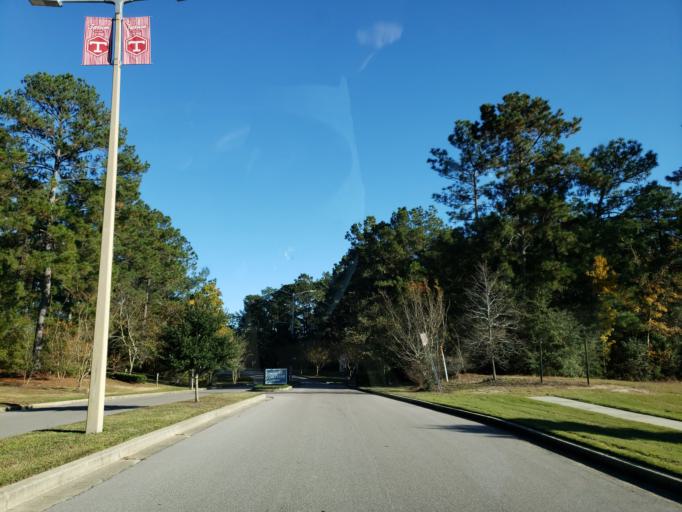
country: US
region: Mississippi
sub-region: Forrest County
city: Hattiesburg
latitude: 31.2806
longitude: -89.3231
